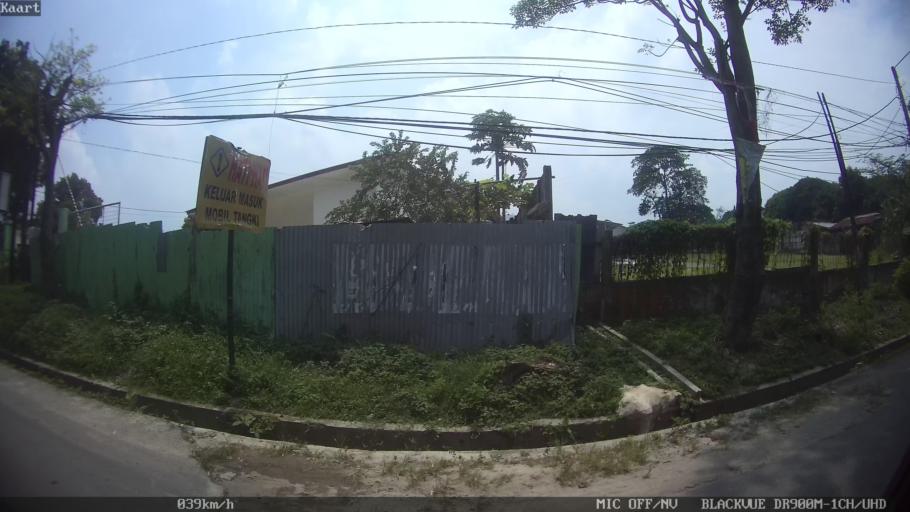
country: ID
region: Lampung
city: Bandarlampung
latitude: -5.4396
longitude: 105.2892
